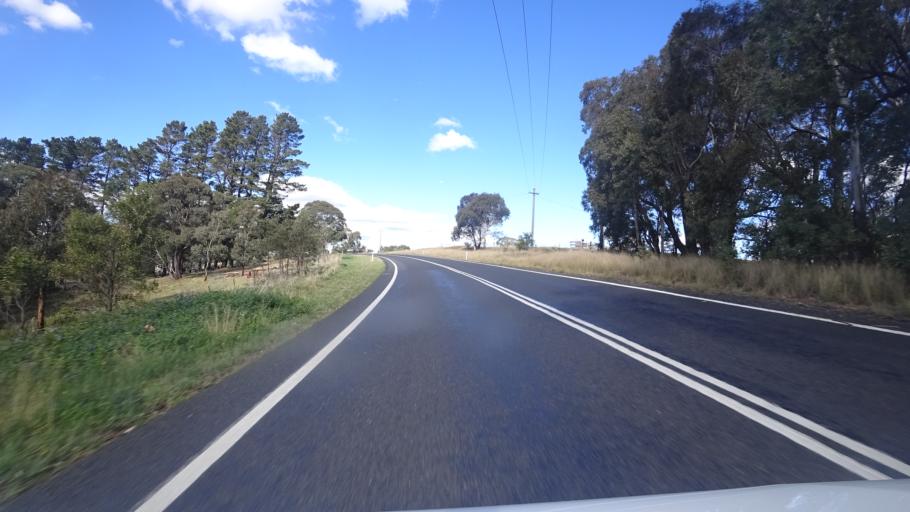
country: AU
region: New South Wales
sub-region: Lithgow
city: Bowenfels
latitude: -33.6374
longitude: 150.0699
